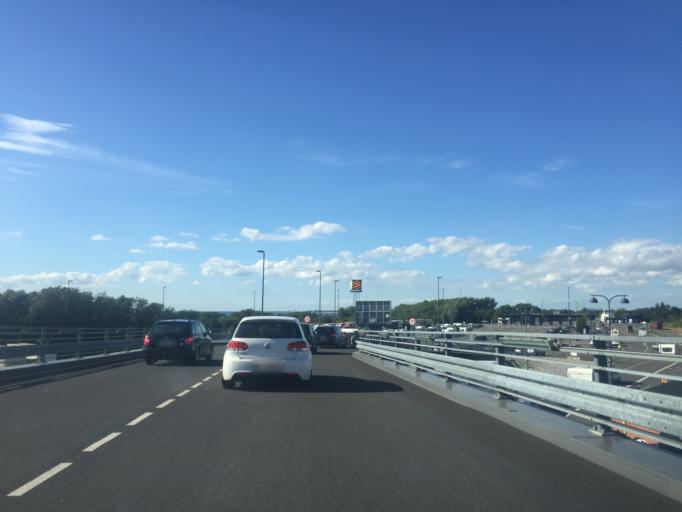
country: DK
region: Zealand
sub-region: Guldborgsund Kommune
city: Nykobing Falster
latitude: 54.5739
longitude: 11.9245
